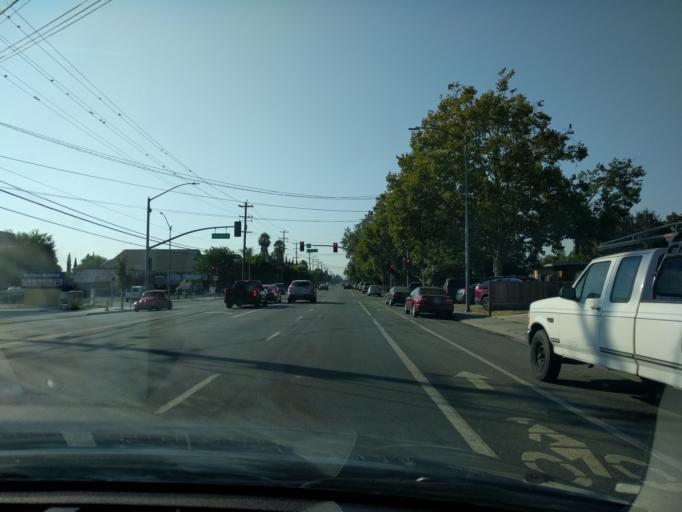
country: US
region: California
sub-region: Santa Clara County
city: Alum Rock
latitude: 37.3594
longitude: -121.8221
